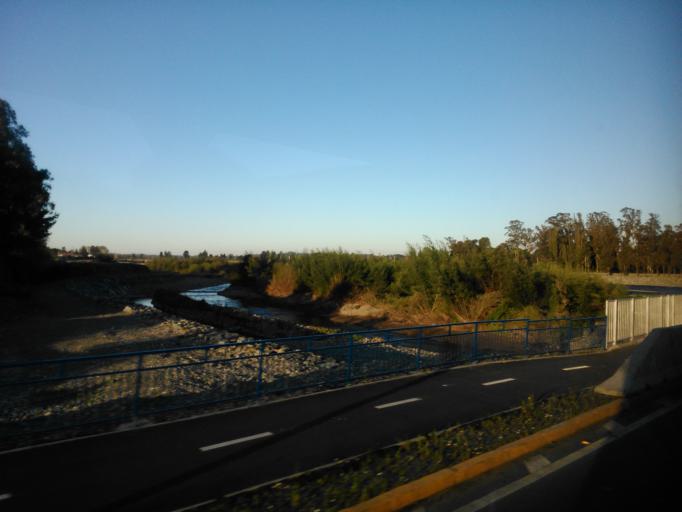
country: CL
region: Araucania
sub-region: Provincia de Cautin
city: Lautaro
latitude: -38.5423
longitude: -72.4373
